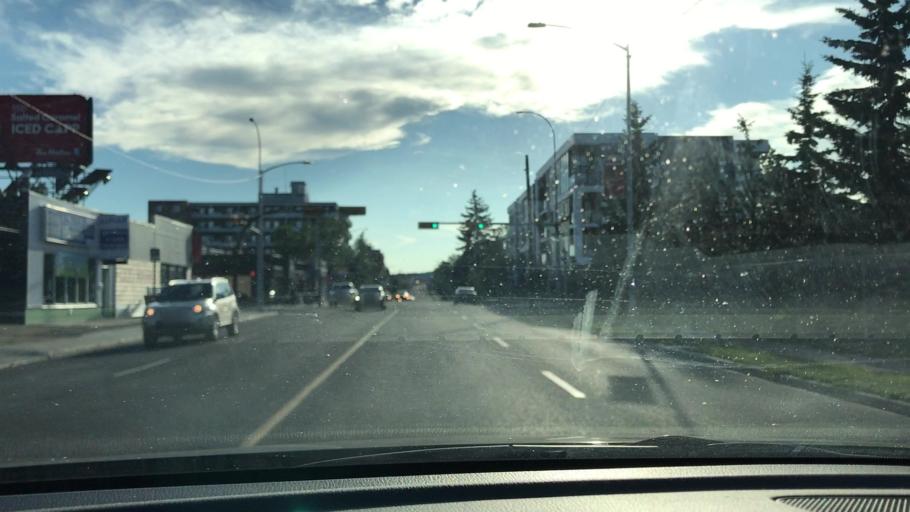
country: CA
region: Alberta
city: Calgary
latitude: 51.0378
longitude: -114.1229
